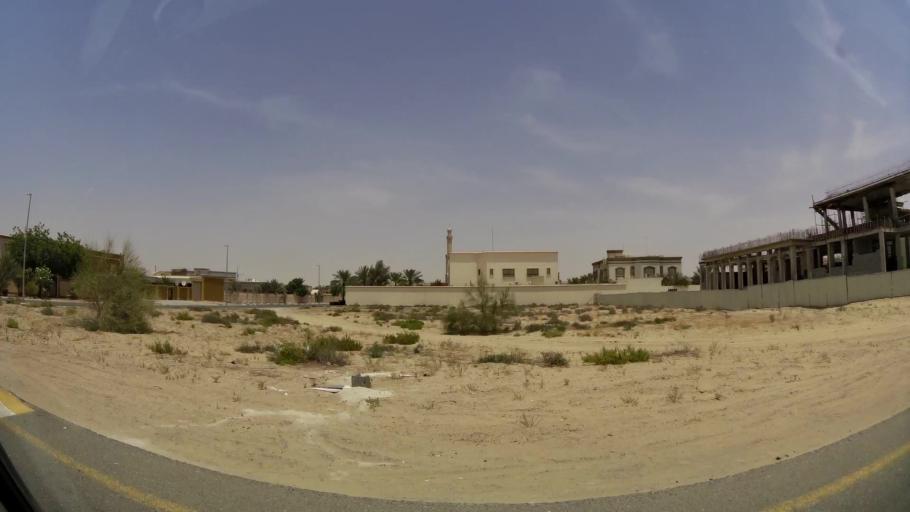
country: AE
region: Ash Shariqah
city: Sharjah
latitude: 25.2521
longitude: 55.4640
